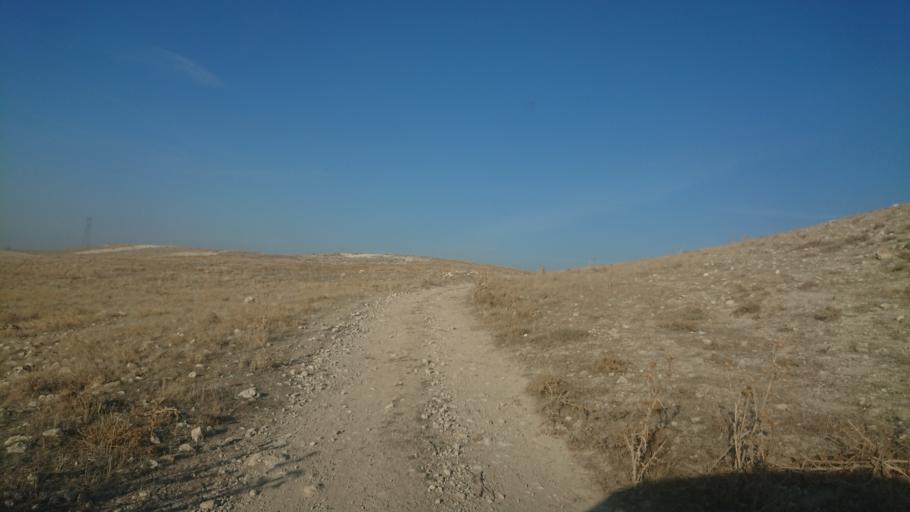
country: TR
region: Aksaray
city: Sultanhani
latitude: 38.1445
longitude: 33.5847
